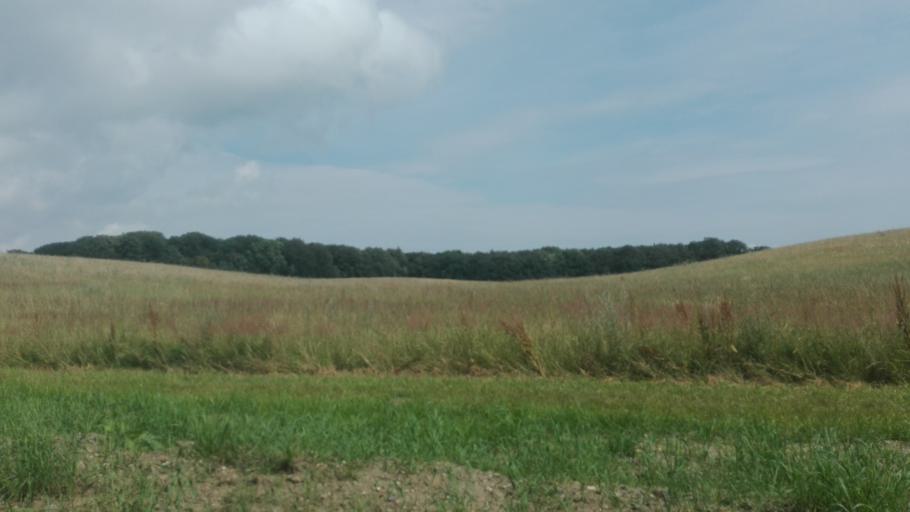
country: DK
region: Central Jutland
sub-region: Arhus Kommune
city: Beder
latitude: 56.0911
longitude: 10.2213
